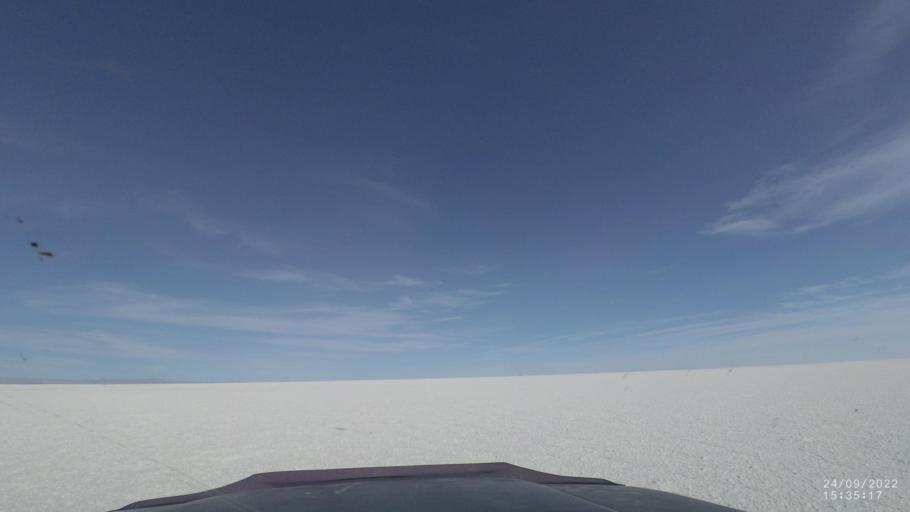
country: BO
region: Potosi
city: Colchani
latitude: -20.1334
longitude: -67.2554
